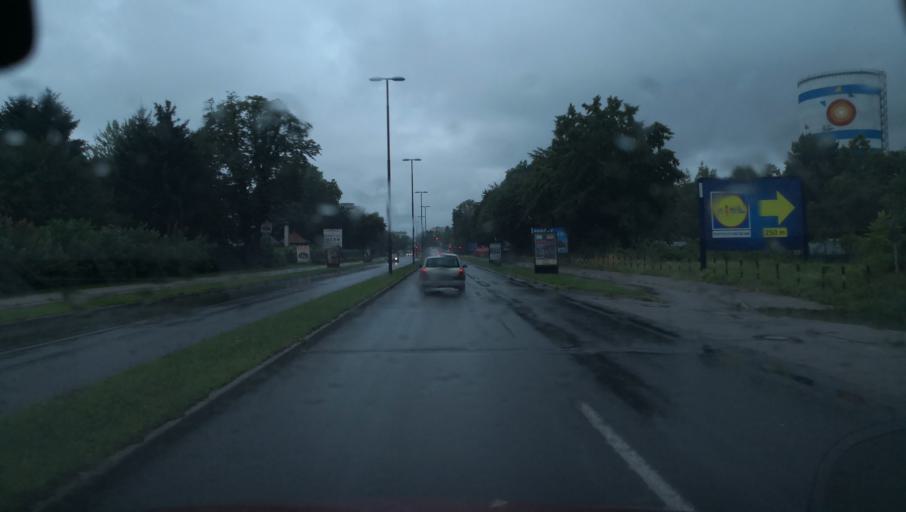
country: SI
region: Ljubljana
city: Ljubljana
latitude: 46.0561
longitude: 14.5485
